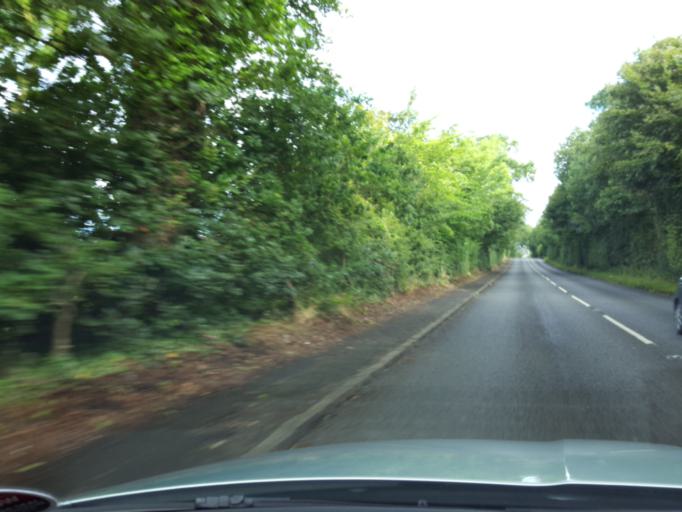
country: GB
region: Scotland
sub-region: Falkirk
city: Bo'ness
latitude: 55.9987
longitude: -3.6084
